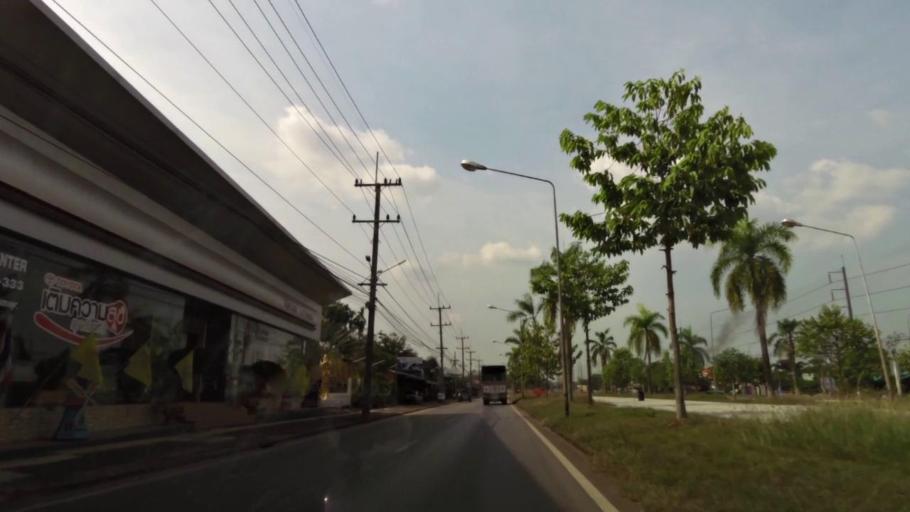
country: TH
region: Rayong
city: Klaeng
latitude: 12.7934
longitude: 101.6448
